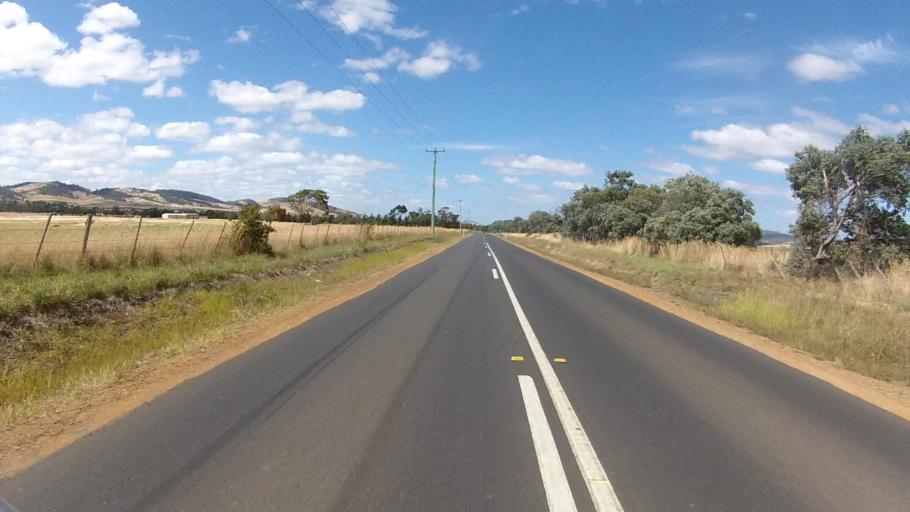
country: AU
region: Tasmania
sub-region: Clarence
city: Cambridge
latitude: -42.7127
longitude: 147.4304
